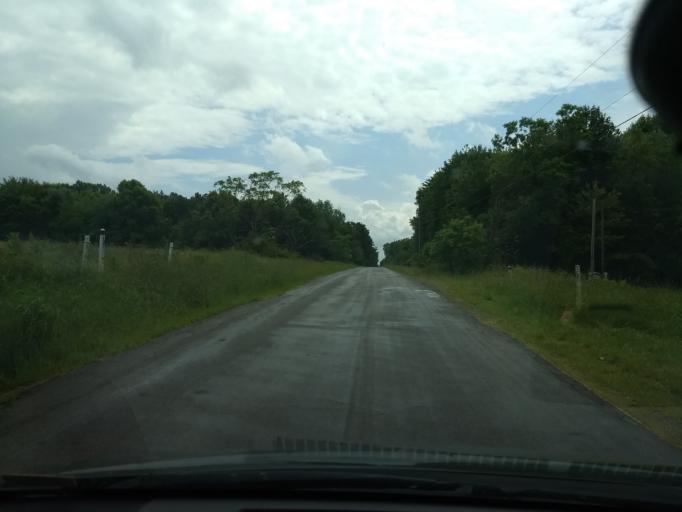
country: US
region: Pennsylvania
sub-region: Armstrong County
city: Orchard Hills
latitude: 40.5591
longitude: -79.5104
